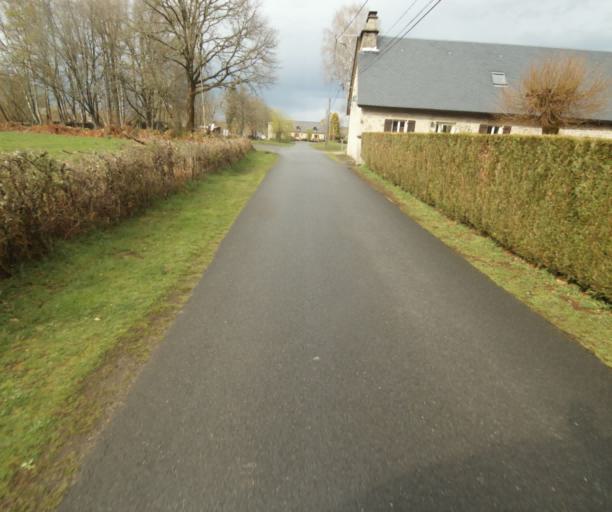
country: FR
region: Limousin
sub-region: Departement de la Correze
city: Saint-Privat
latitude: 45.2414
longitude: 2.0067
